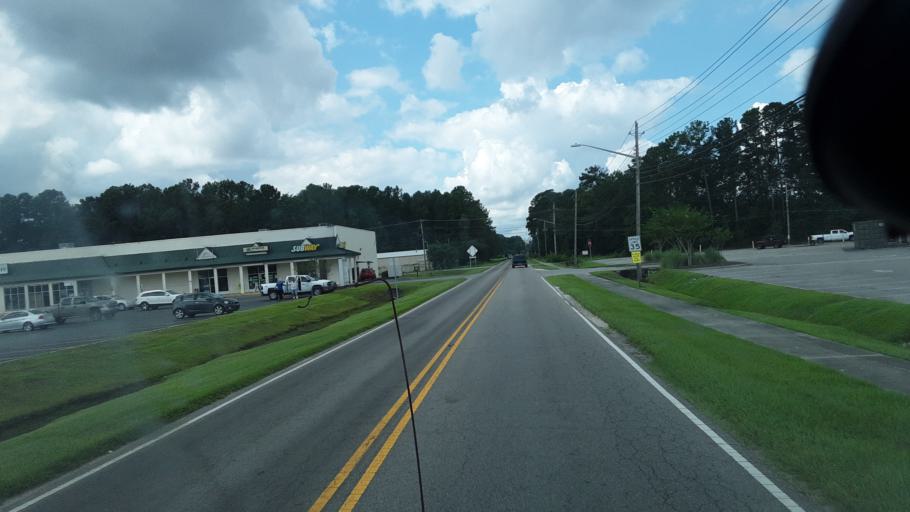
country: US
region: South Carolina
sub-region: Georgetown County
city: Georgetown
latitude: 33.3893
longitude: -79.2901
